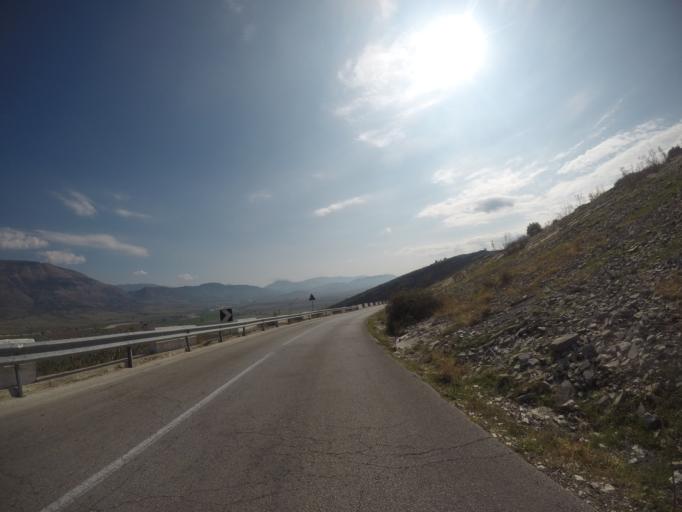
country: AL
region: Gjirokaster
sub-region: Rrethi i Gjirokastres
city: Libohove
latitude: 39.9483
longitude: 20.2495
